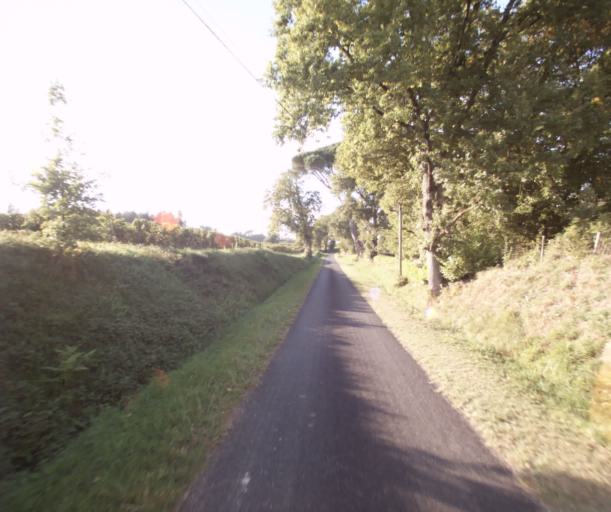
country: FR
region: Midi-Pyrenees
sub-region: Departement du Gers
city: Eauze
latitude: 43.8572
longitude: 0.0133
